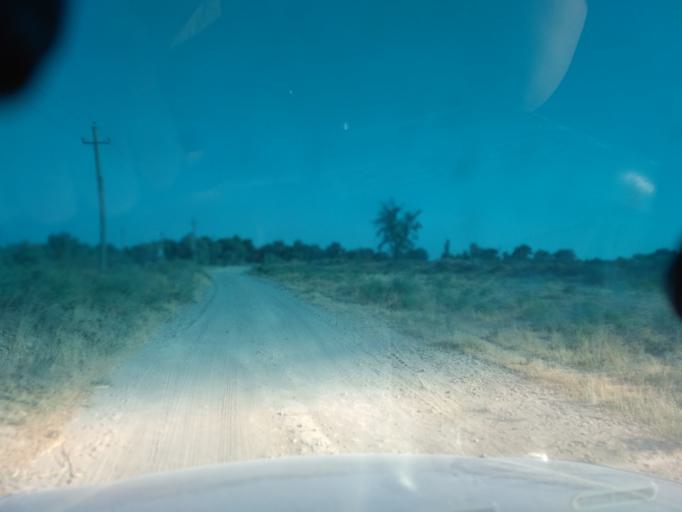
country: TJ
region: Viloyati Sughd
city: Buston
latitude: 40.5577
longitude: 69.0751
